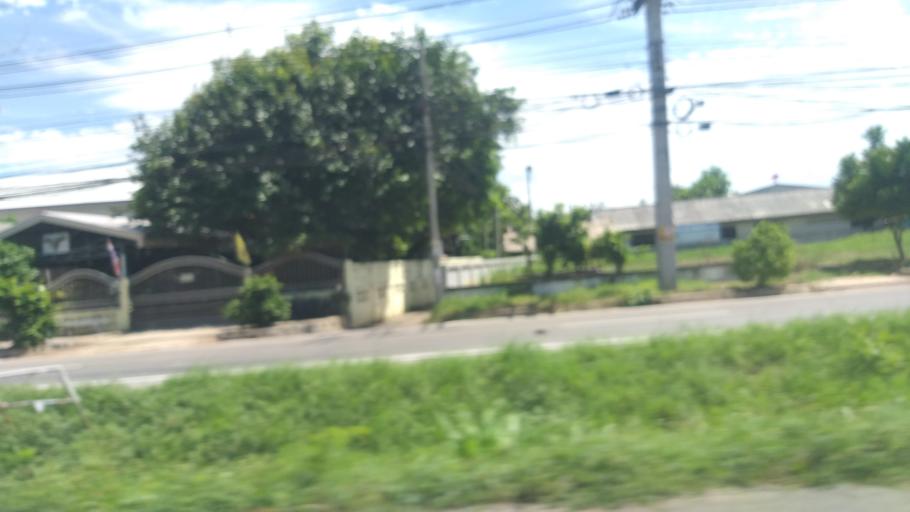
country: TH
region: Khon Kaen
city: Ban Fang
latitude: 16.4484
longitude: 102.6452
